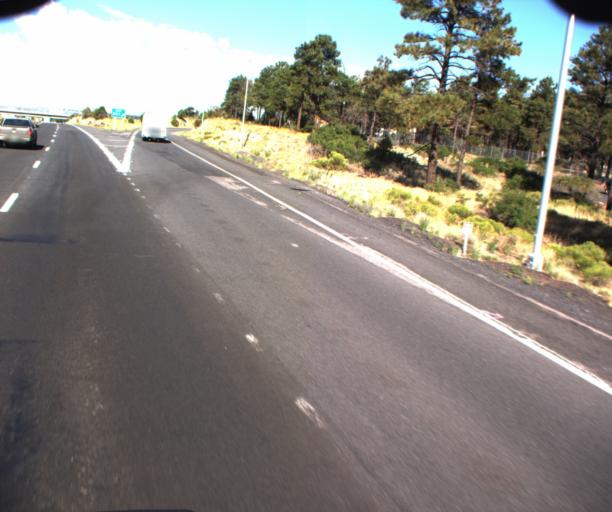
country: US
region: Arizona
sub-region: Coconino County
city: Flagstaff
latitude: 35.2179
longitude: -111.5779
